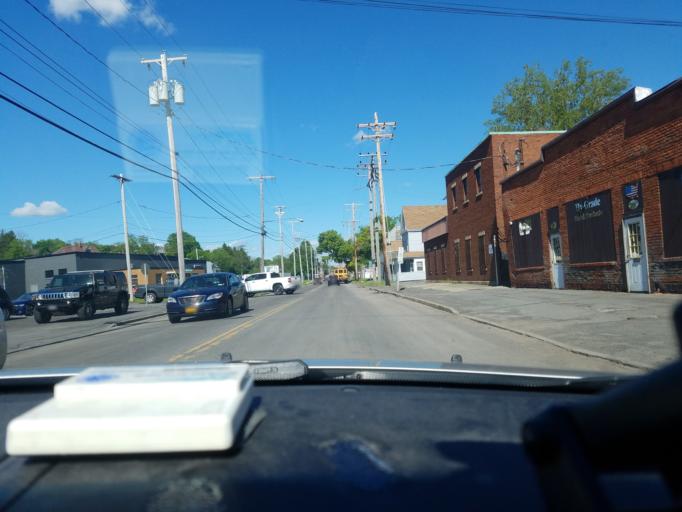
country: US
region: New York
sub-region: Onondaga County
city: Syracuse
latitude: 43.0528
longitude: -76.1272
